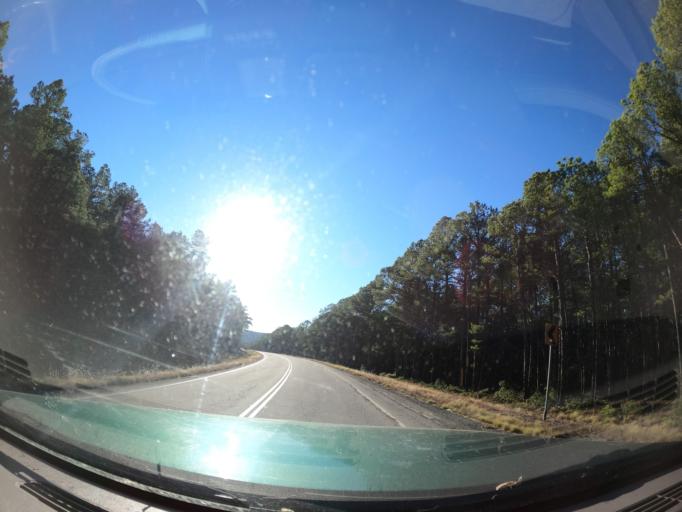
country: US
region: Oklahoma
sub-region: Latimer County
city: Wilburton
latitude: 35.0007
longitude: -95.3412
